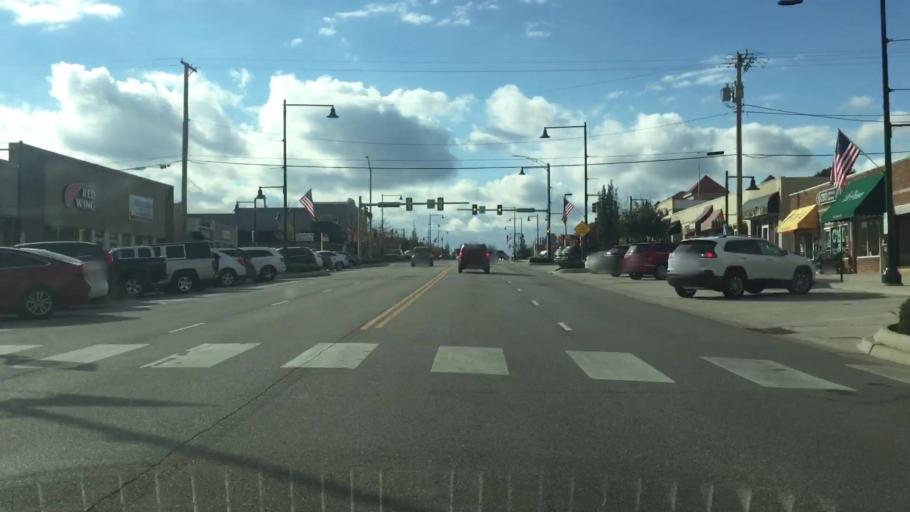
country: US
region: Kansas
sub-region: Johnson County
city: Mission
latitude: 39.0221
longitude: -94.6526
